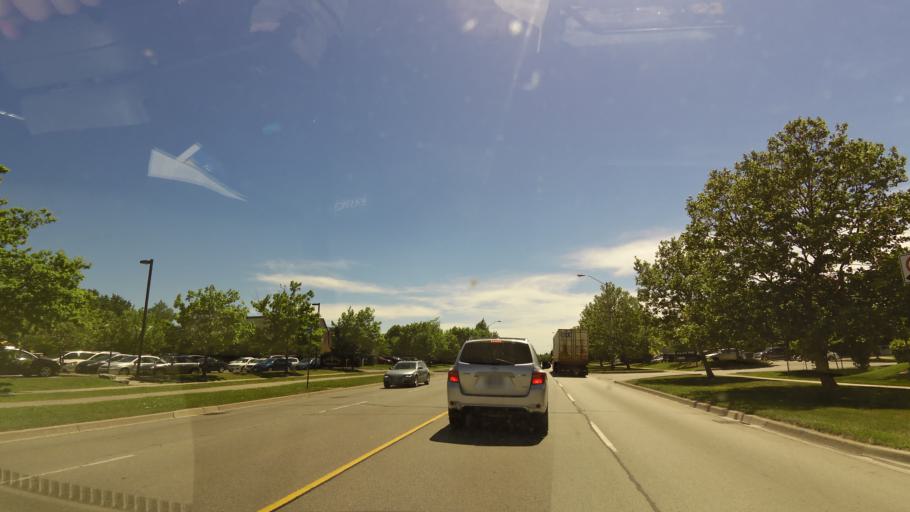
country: CA
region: Ontario
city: Oakville
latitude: 43.4778
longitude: -79.6599
